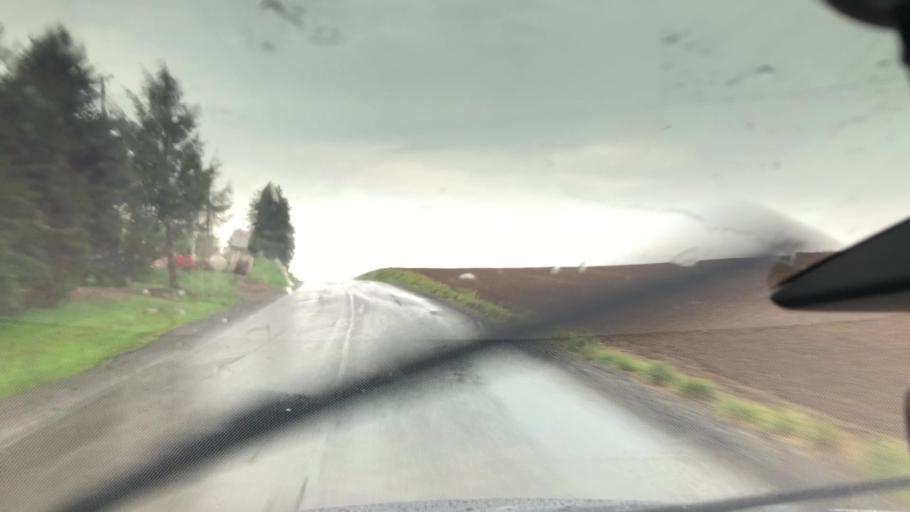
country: US
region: Pennsylvania
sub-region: Butler County
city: Saxonburg
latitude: 40.7498
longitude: -79.8577
